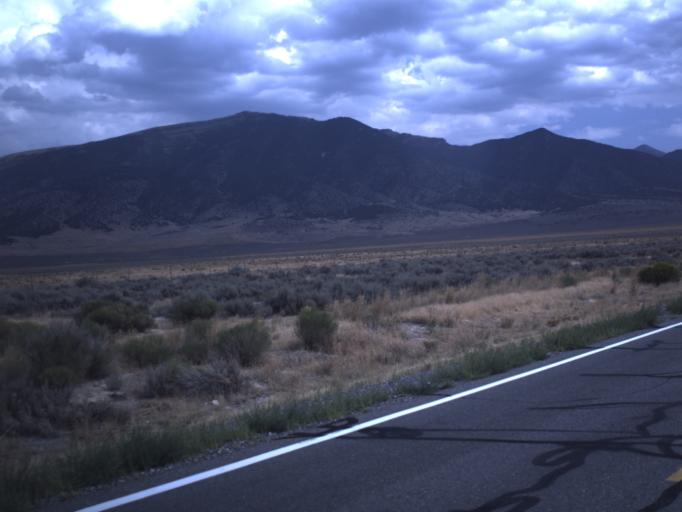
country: US
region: Utah
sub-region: Tooele County
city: Tooele
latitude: 40.3735
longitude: -112.3653
